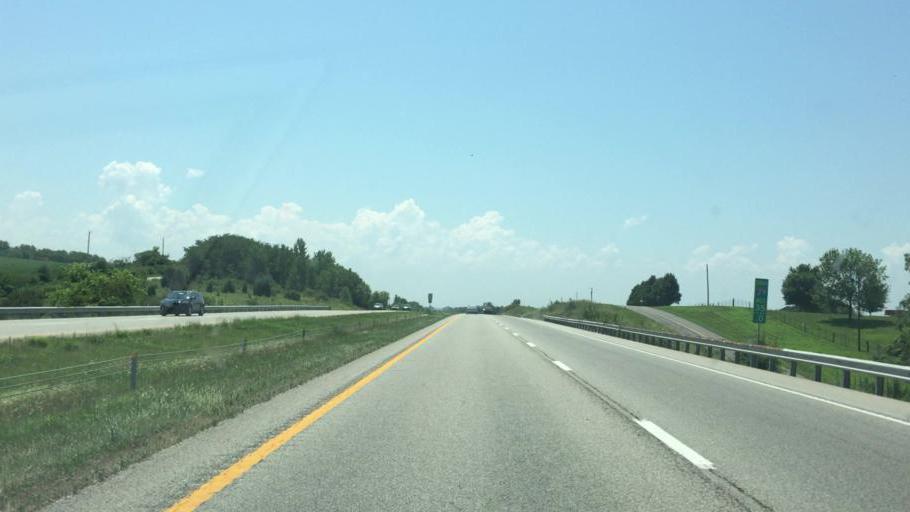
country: US
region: Kansas
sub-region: Doniphan County
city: Elwood
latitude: 39.5898
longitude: -94.7890
